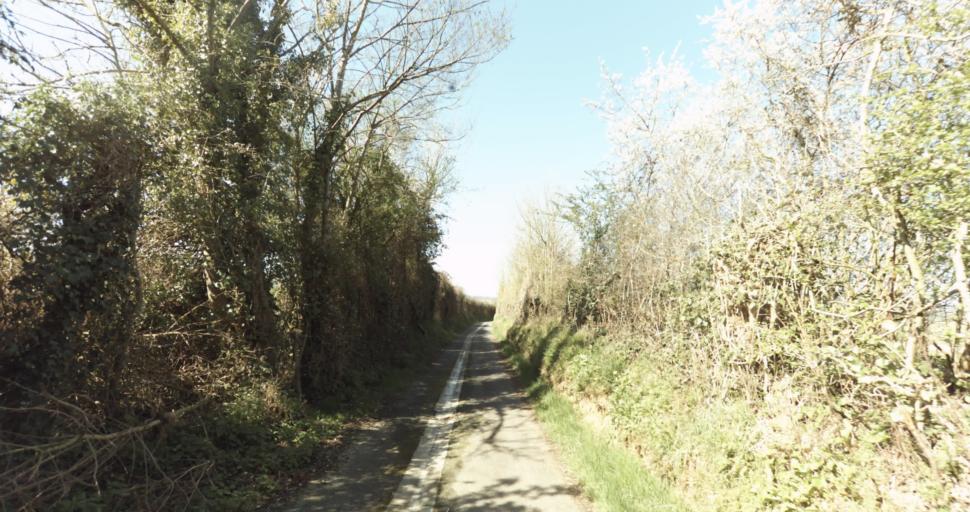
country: FR
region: Lower Normandy
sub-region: Departement du Calvados
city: Saint-Pierre-sur-Dives
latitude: 49.0066
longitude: 0.0331
